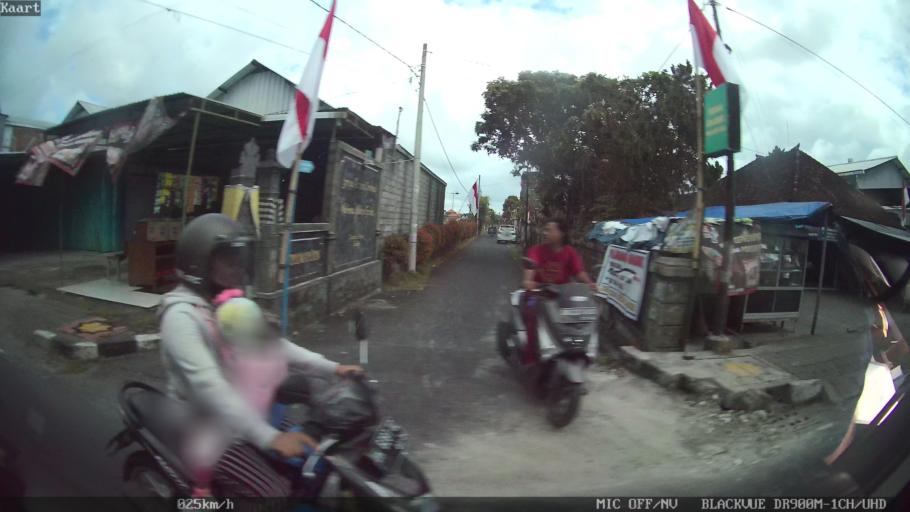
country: ID
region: Bali
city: Banjar Karangsuling
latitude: -8.6013
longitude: 115.1726
